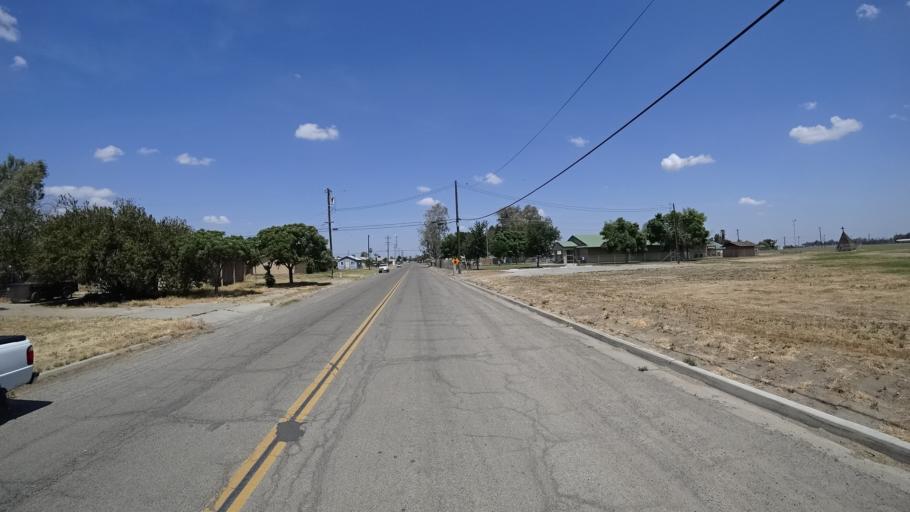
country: US
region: California
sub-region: Kings County
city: Stratford
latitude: 36.1873
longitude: -119.8205
